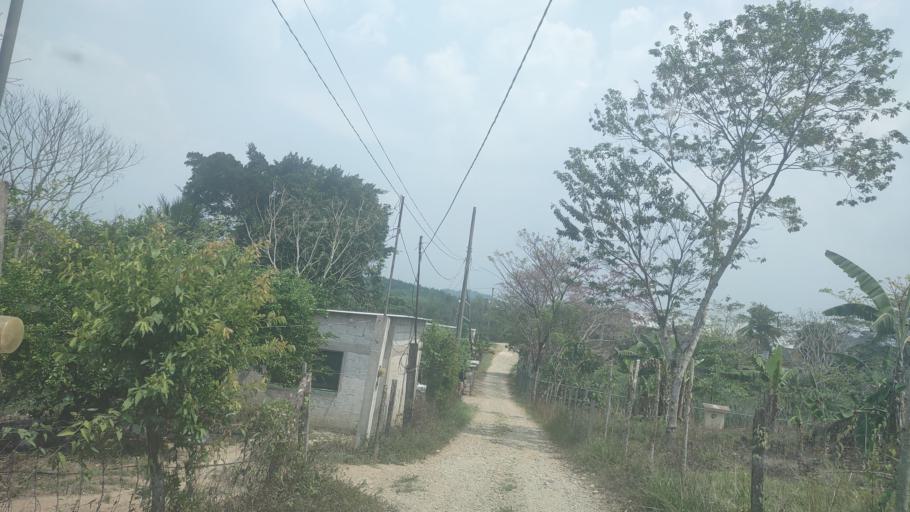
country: MX
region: Tabasco
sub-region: Huimanguillo
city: Francisco Rueda
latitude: 17.6684
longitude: -93.8856
